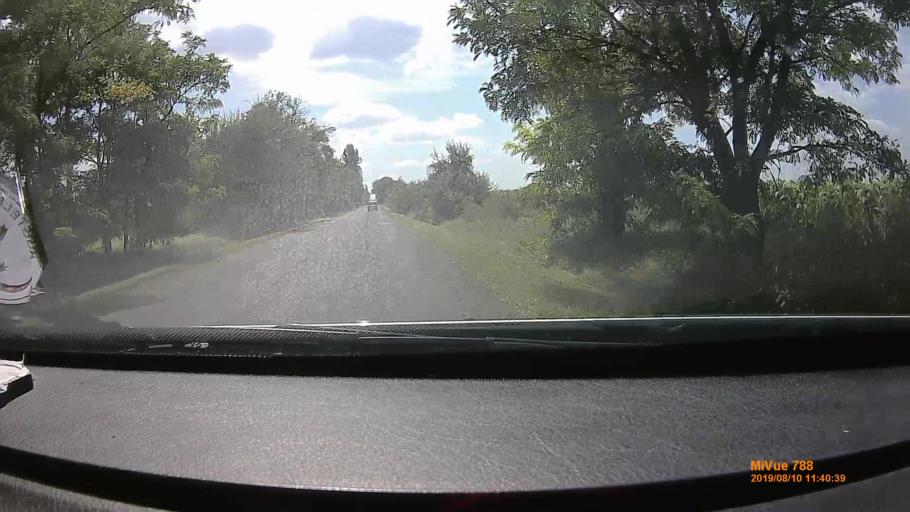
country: HU
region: Borsod-Abauj-Zemplen
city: Mezokovesd
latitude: 47.7581
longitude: 20.6039
